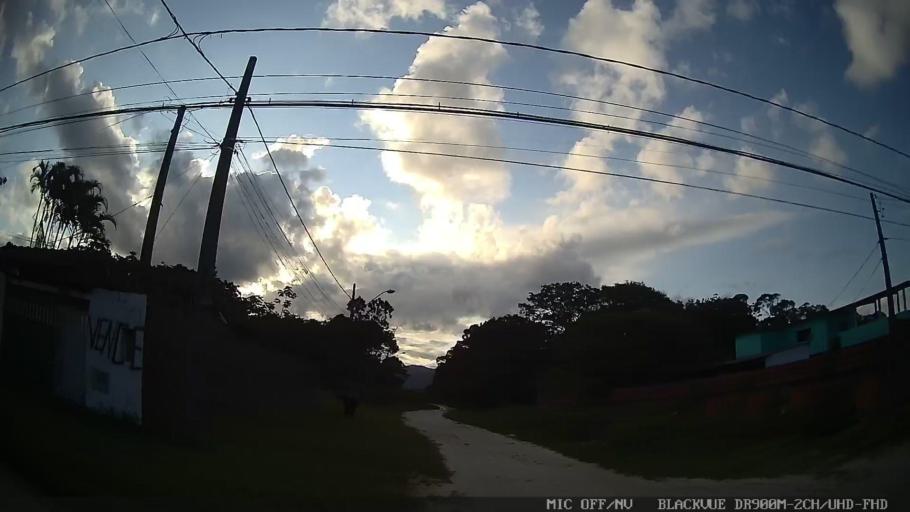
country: BR
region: Sao Paulo
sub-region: Itanhaem
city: Itanhaem
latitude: -24.1590
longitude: -46.8301
